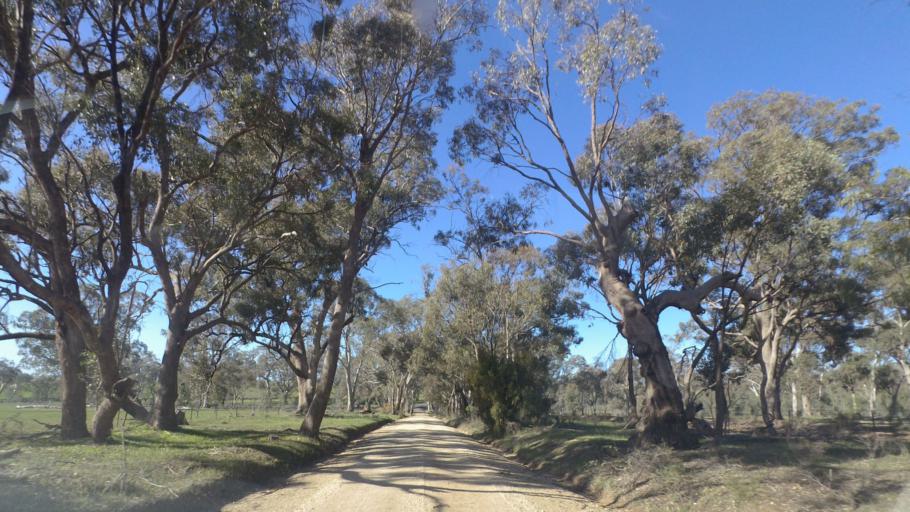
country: AU
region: Victoria
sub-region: Mount Alexander
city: Castlemaine
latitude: -36.9683
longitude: 144.3517
